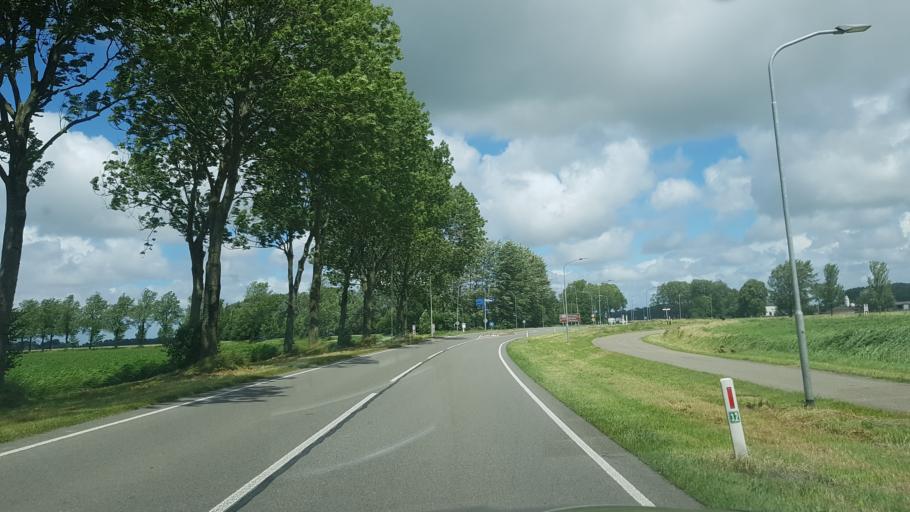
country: NL
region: Groningen
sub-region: Gemeente Winsum
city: Winsum
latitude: 53.3697
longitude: 6.5142
